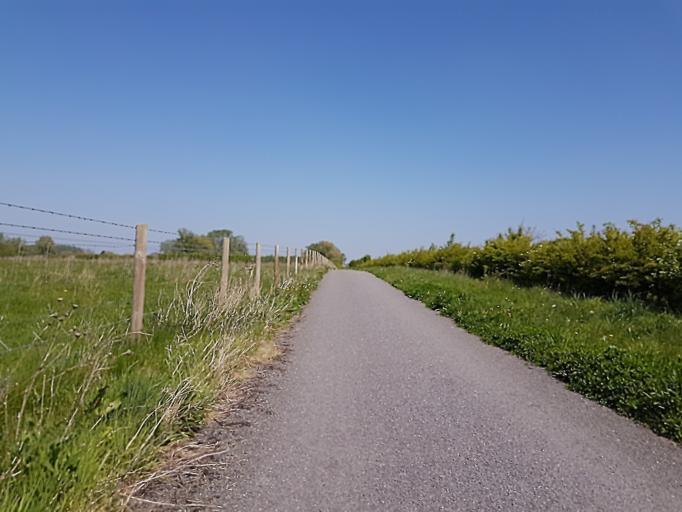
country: GB
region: England
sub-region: Cambridgeshire
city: Harston
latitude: 52.1570
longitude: 0.0912
